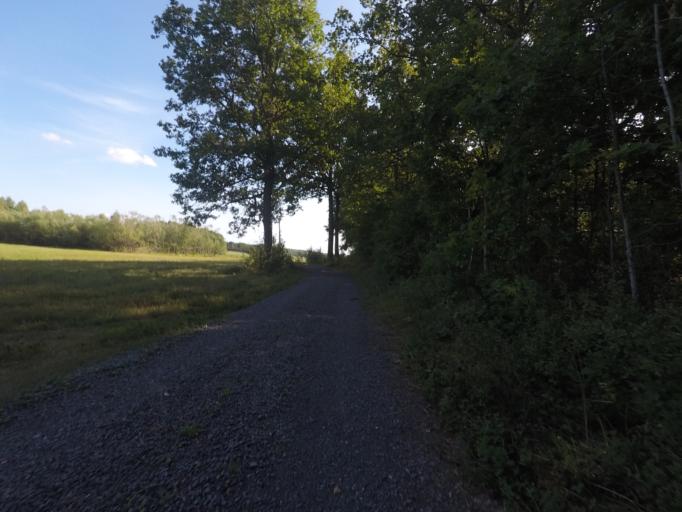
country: SE
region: Soedermanland
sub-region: Eskilstuna Kommun
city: Kvicksund
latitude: 59.4440
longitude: 16.2702
